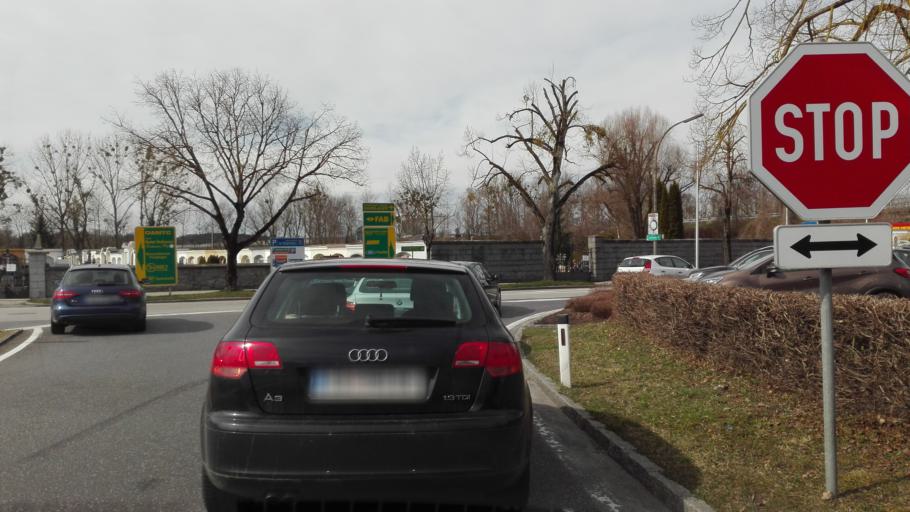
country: AT
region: Upper Austria
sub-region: Politischer Bezirk Scharding
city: Scharding
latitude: 48.4614
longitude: 13.4341
